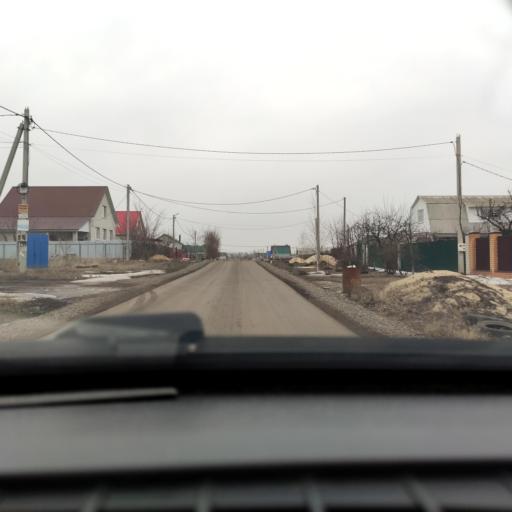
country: RU
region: Voronezj
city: Novaya Usman'
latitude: 51.6590
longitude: 39.4142
